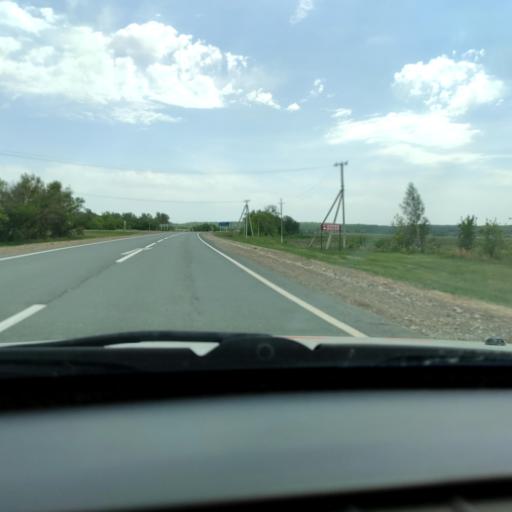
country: RU
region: Samara
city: Mirnyy
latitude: 53.6304
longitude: 50.2454
